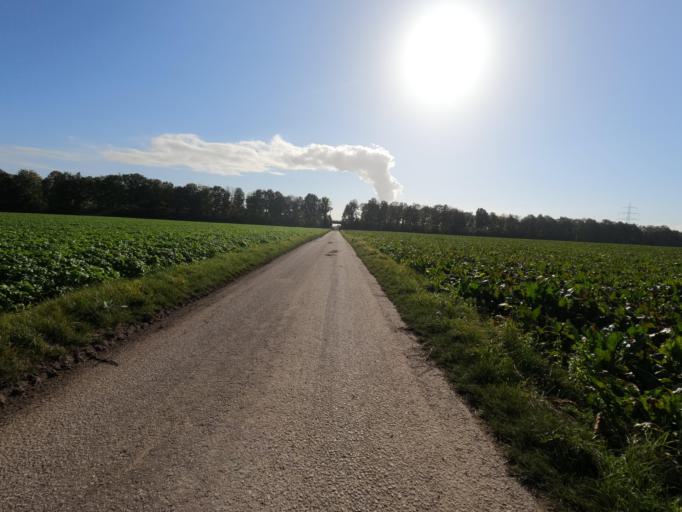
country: DE
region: North Rhine-Westphalia
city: Neu-Pattern
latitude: 50.8966
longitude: 6.2696
